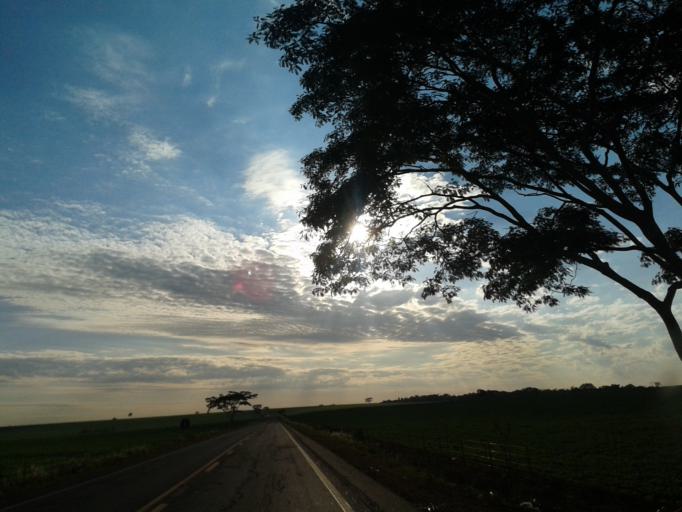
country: BR
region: Minas Gerais
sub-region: Capinopolis
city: Capinopolis
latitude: -18.6848
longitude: -49.5317
